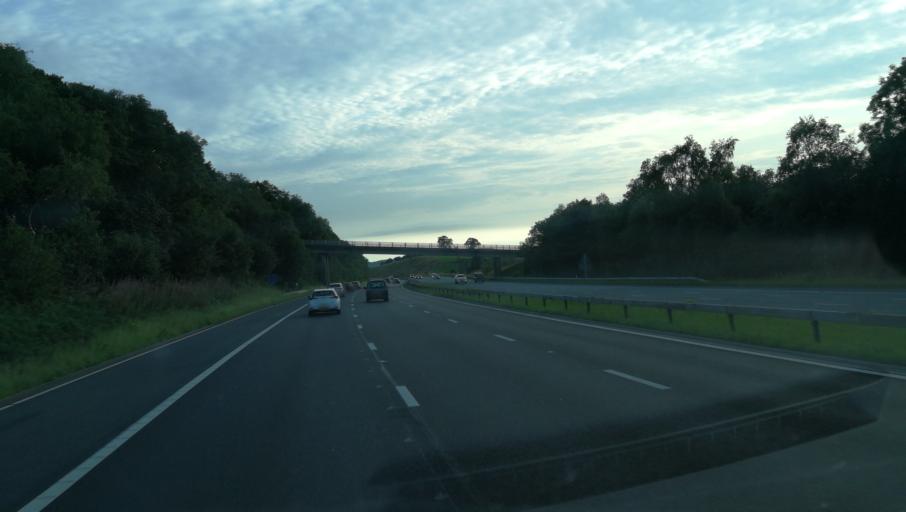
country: GB
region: England
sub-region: Cumbria
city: Milnthorpe
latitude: 54.2566
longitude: -2.6889
